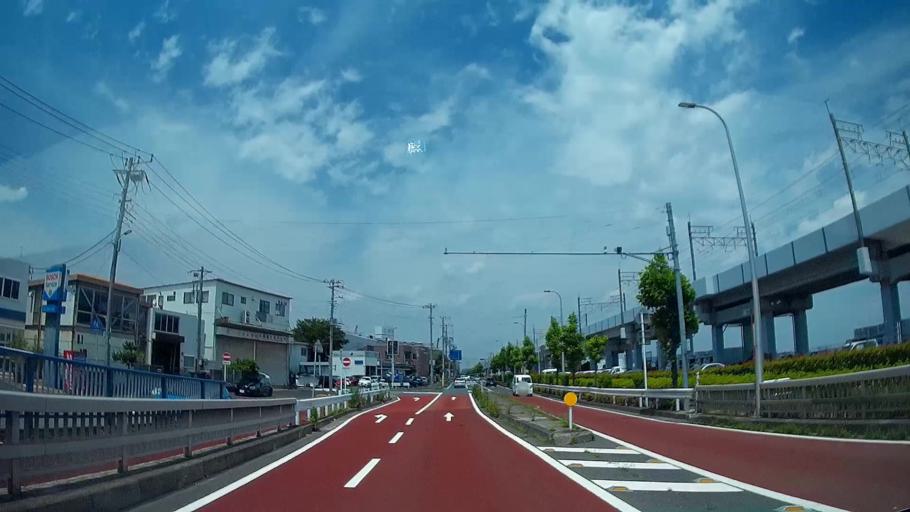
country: JP
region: Tokyo
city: Urayasu
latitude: 35.6567
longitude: 139.9182
